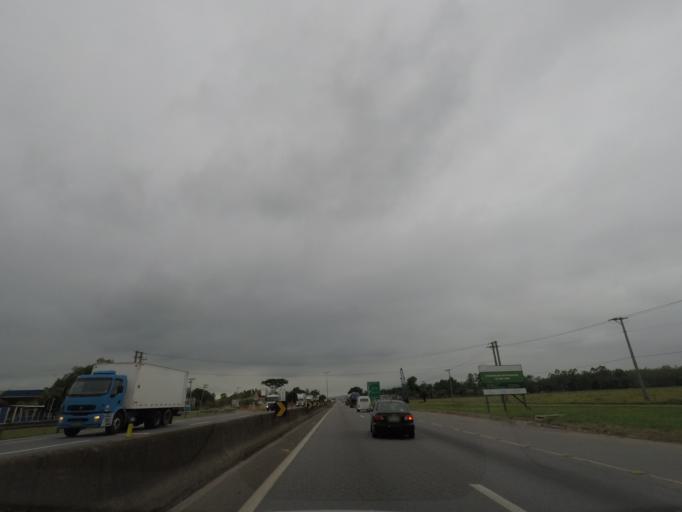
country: BR
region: Sao Paulo
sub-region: Pindamonhangaba
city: Pindamonhangaba
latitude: -22.9281
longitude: -45.3566
